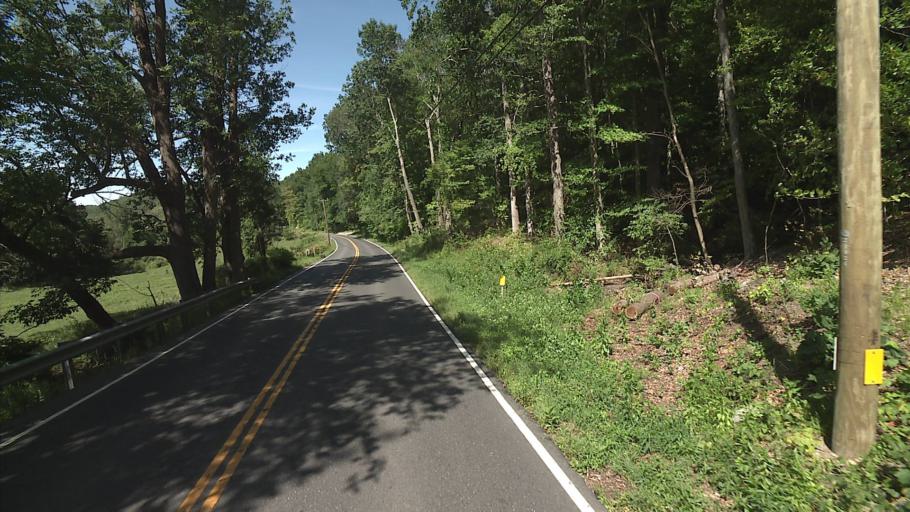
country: US
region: Connecticut
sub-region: New Haven County
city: Oxford
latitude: 41.4417
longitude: -73.1557
